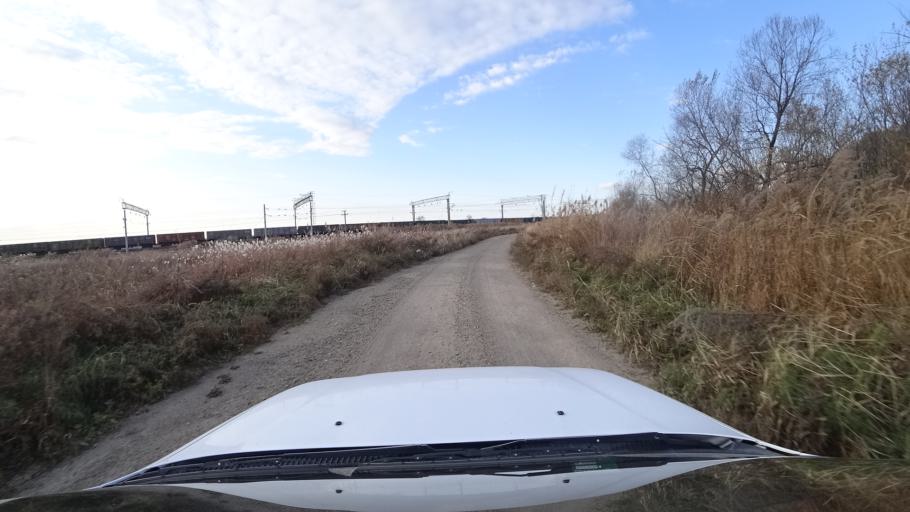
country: RU
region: Primorskiy
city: Lazo
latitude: 45.8180
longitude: 133.6102
